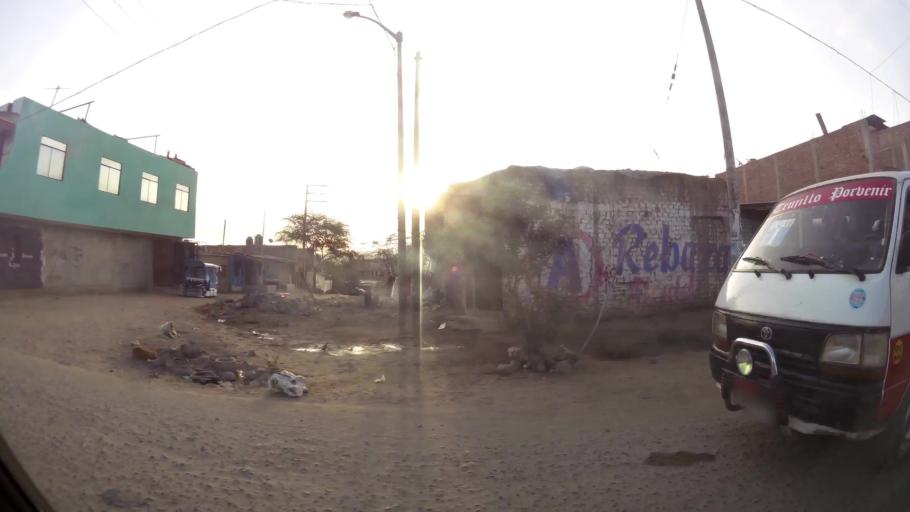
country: PE
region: La Libertad
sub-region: Provincia de Trujillo
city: El Porvenir
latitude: -8.0715
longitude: -78.9976
